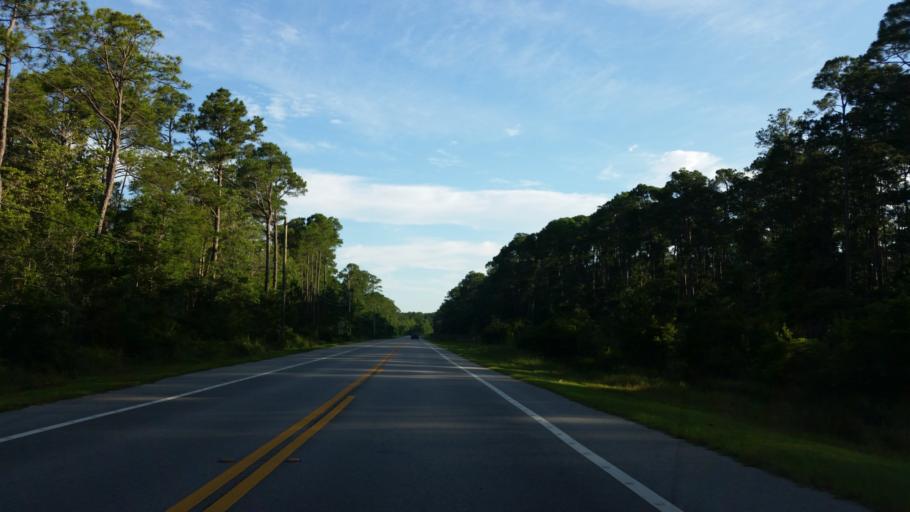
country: US
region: Florida
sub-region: Escambia County
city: Warrington
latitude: 30.3444
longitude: -87.3423
